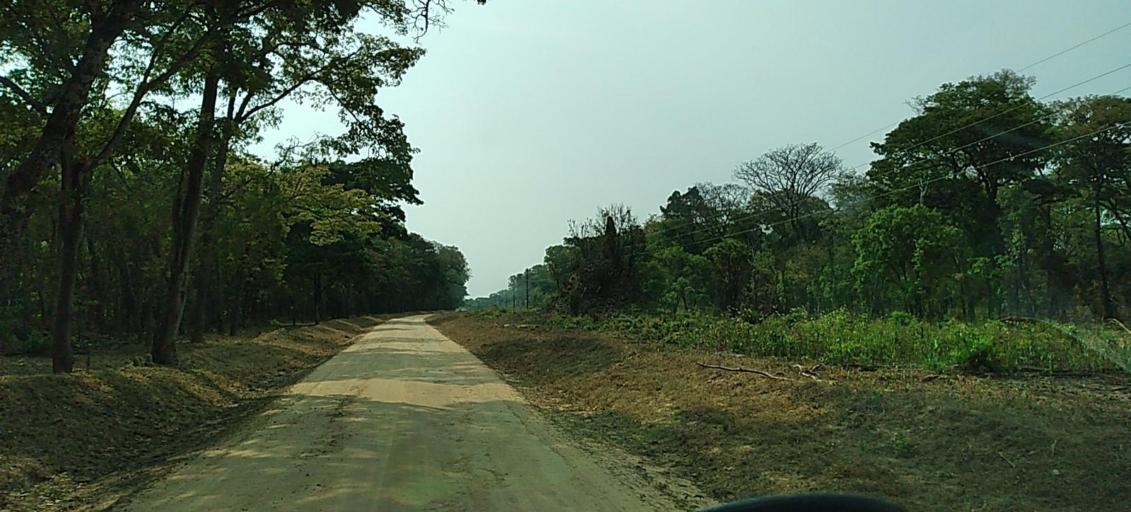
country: ZM
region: North-Western
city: Solwezi
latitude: -12.6911
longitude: 26.4007
